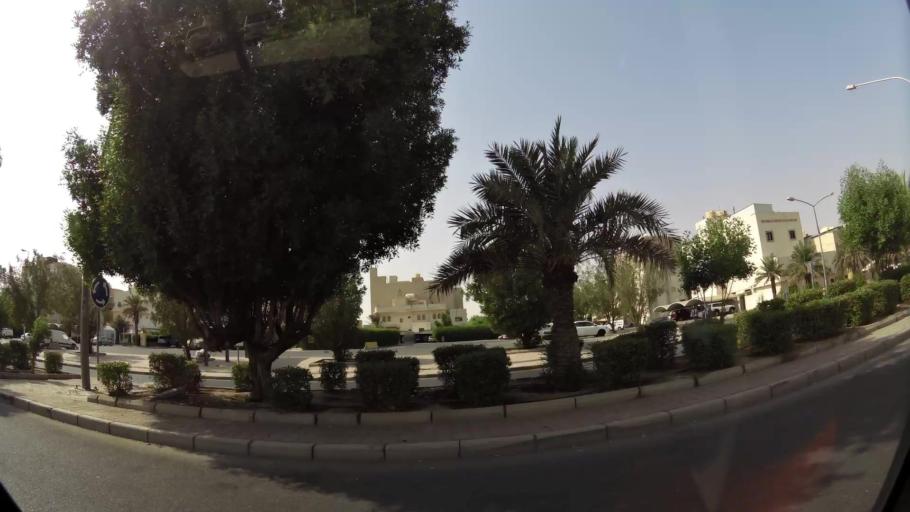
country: KW
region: Muhafazat al Jahra'
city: Al Jahra'
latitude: 29.3335
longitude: 47.6550
